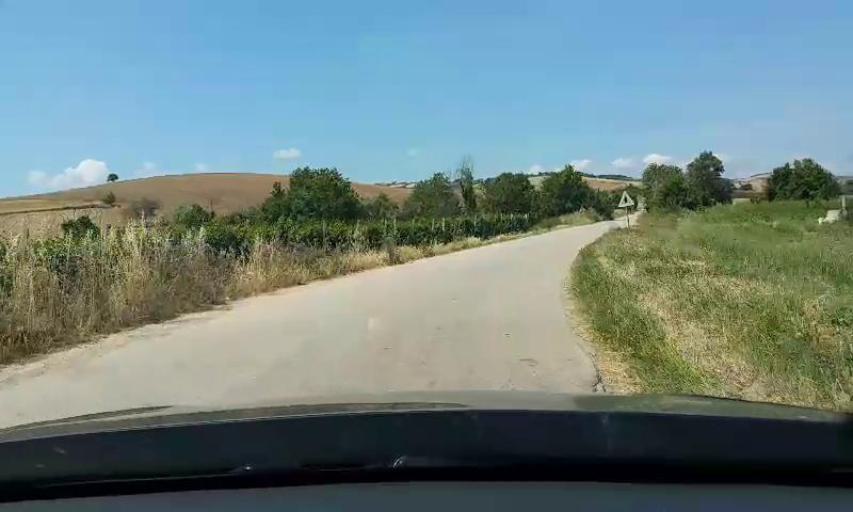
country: IT
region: Molise
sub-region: Provincia di Campobasso
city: Montecilfone
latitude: 41.9257
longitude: 14.8558
